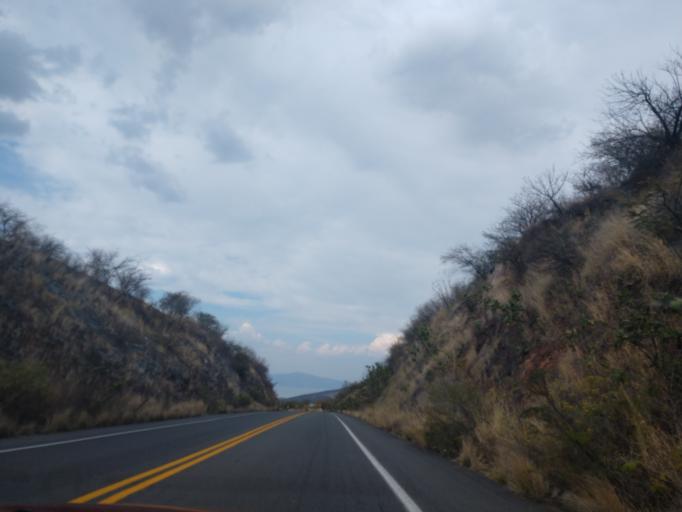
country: MX
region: Jalisco
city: La Manzanilla de la Paz
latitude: 20.1134
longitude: -103.1654
